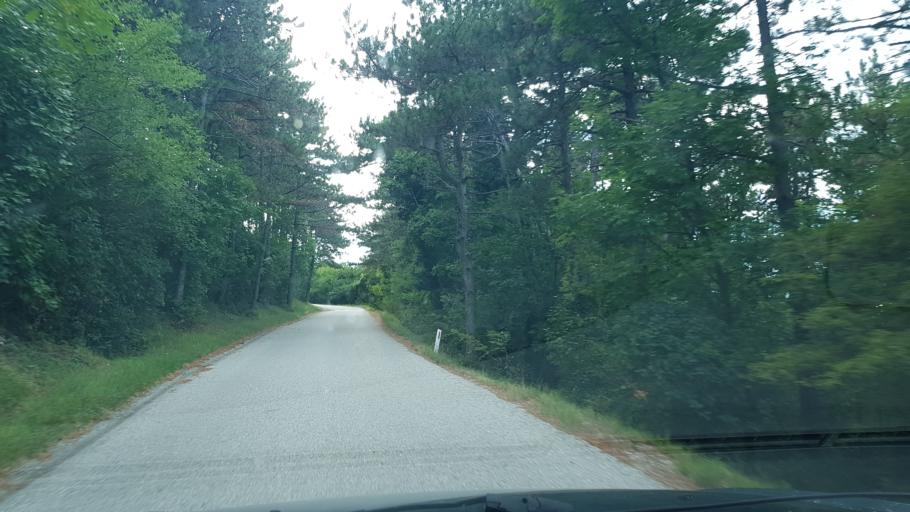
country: SI
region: Rence-Vogrsko
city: Rence
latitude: 45.8703
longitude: 13.6574
